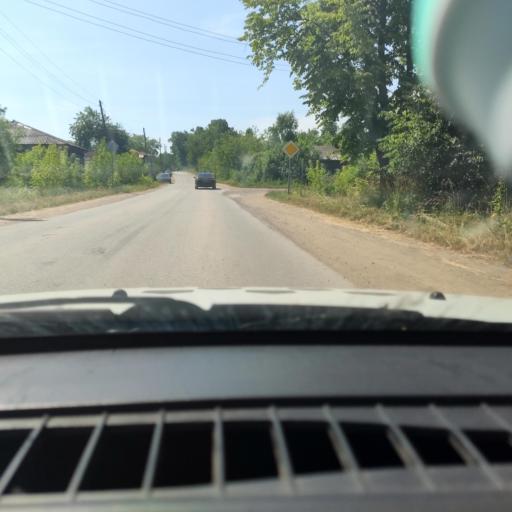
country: RU
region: Perm
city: Okhansk
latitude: 57.7246
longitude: 55.3825
